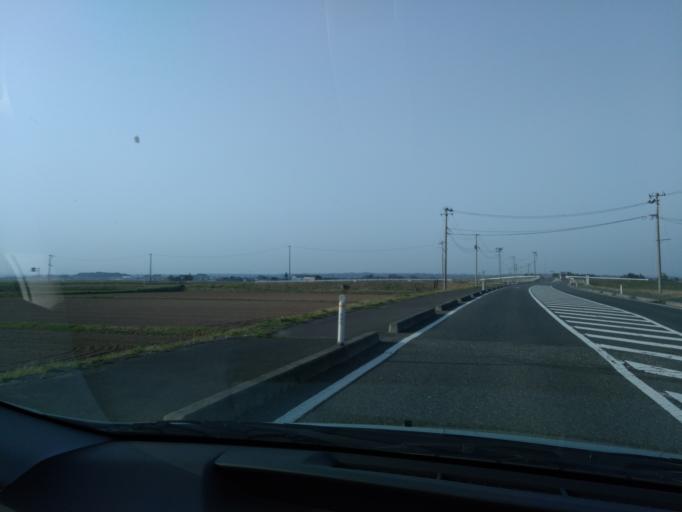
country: JP
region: Iwate
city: Ichinoseki
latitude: 38.7465
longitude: 141.1317
